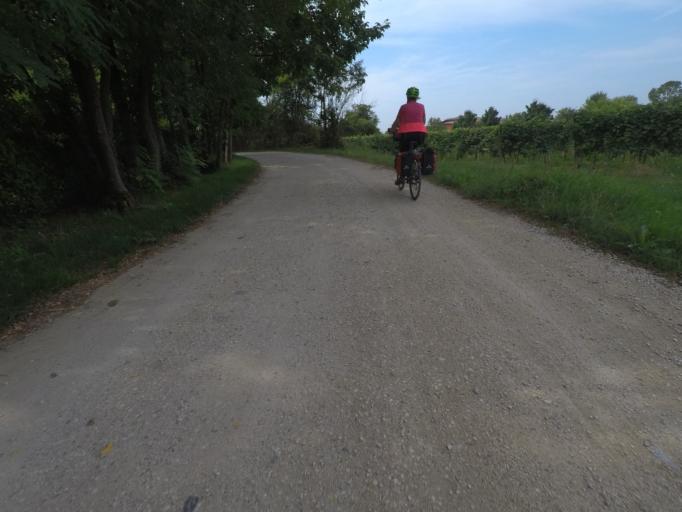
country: IT
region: Veneto
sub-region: Provincia di Treviso
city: Cappella Maggiore
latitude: 45.9683
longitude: 12.3351
